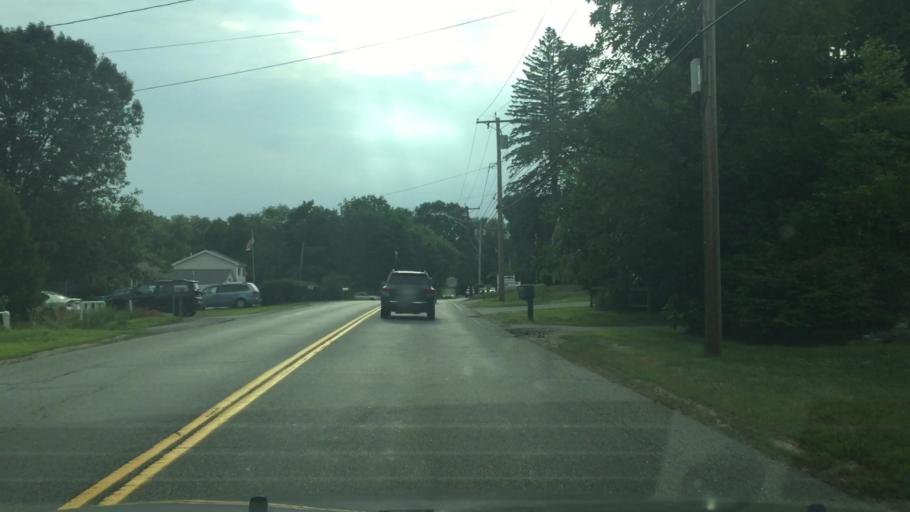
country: US
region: New Hampshire
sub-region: Rockingham County
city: Atkinson
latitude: 42.7896
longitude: -71.1452
